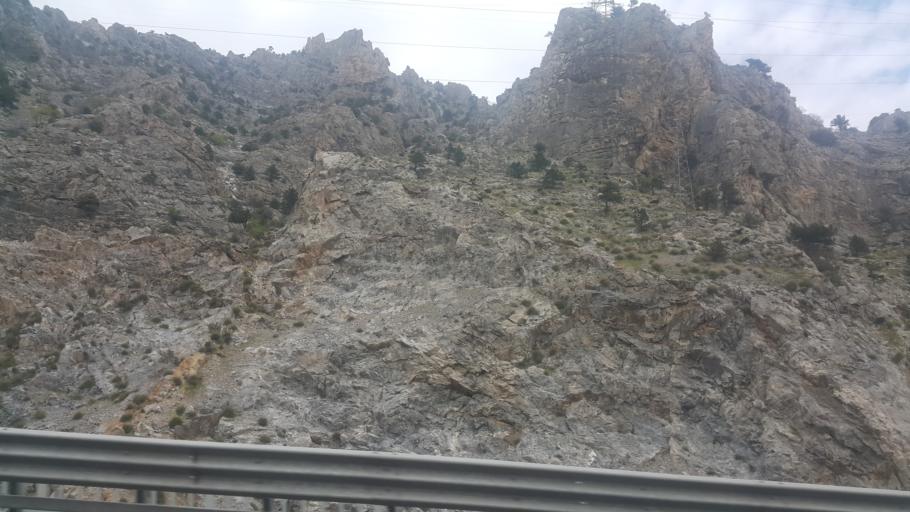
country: TR
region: Adana
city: Pozanti
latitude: 37.4756
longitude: 34.8600
